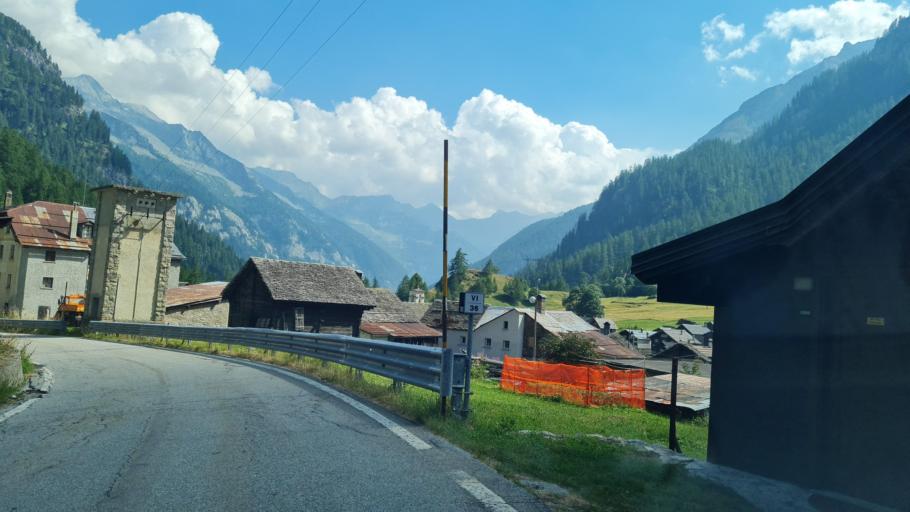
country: IT
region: Piedmont
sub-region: Provincia Verbano-Cusio-Ossola
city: Formazza
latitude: 46.3933
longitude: 8.4197
